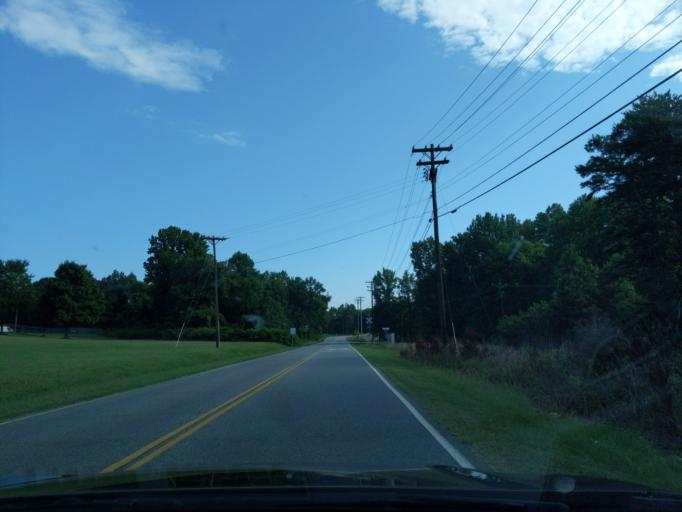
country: US
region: South Carolina
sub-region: Greenville County
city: Mauldin
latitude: 34.8050
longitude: -82.3118
